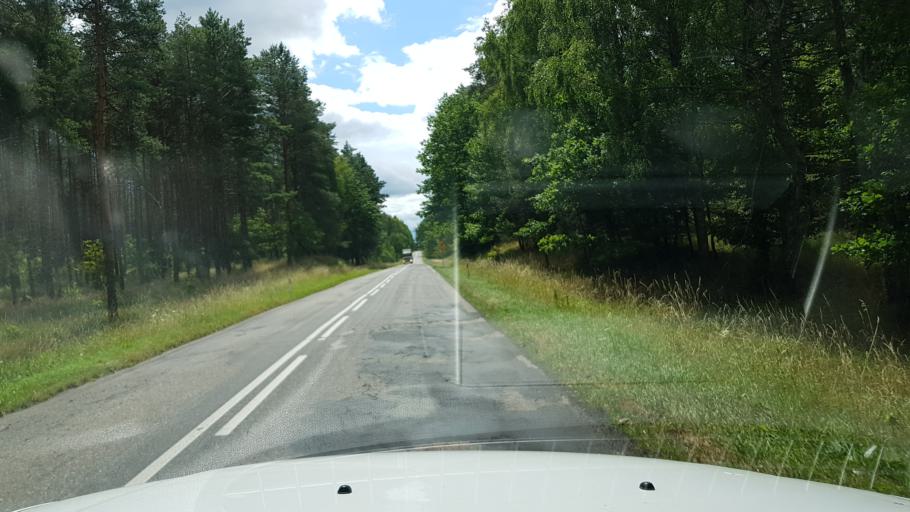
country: PL
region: West Pomeranian Voivodeship
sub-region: Powiat stargardzki
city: Insko
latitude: 53.3630
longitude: 15.5882
